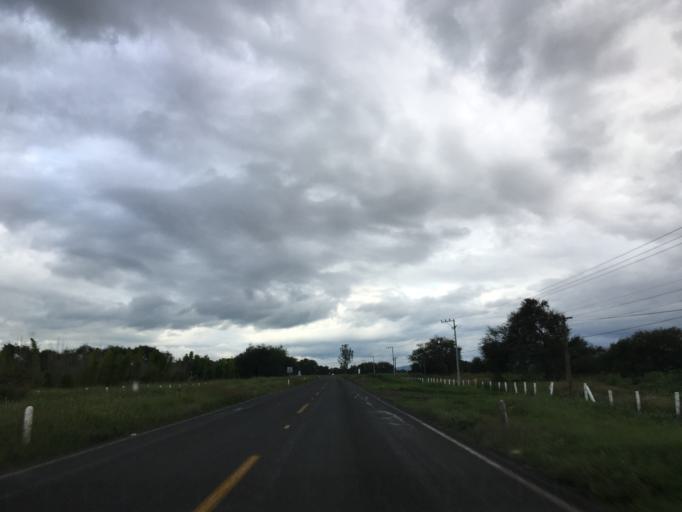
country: MX
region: Michoacan
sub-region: Cuitzeo
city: Cuamio
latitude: 20.0053
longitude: -101.1555
